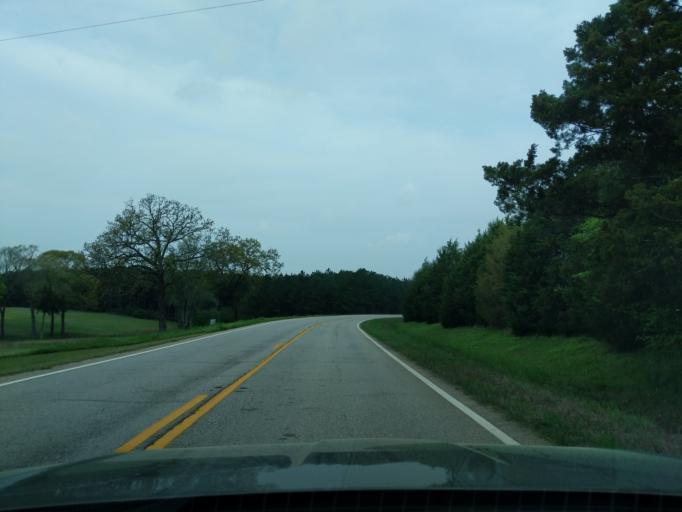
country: US
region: Georgia
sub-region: Lincoln County
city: Lincolnton
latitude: 33.7927
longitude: -82.3831
